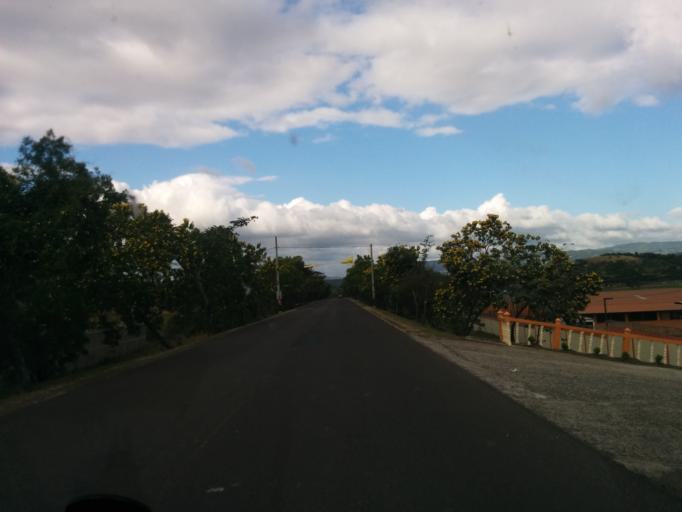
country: NI
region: Esteli
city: Esteli
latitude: 13.1683
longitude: -86.3674
